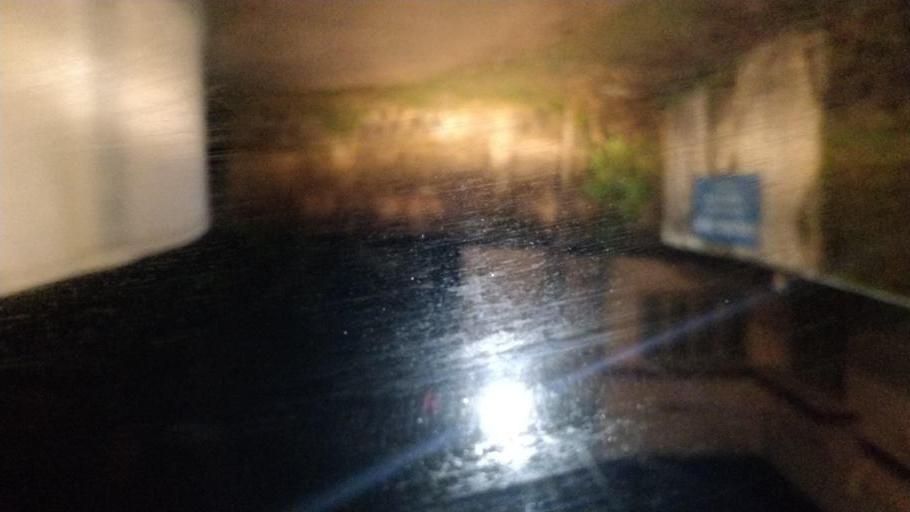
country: IN
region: Kerala
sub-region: Kottayam
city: Kottayam
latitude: 9.6411
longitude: 76.5077
